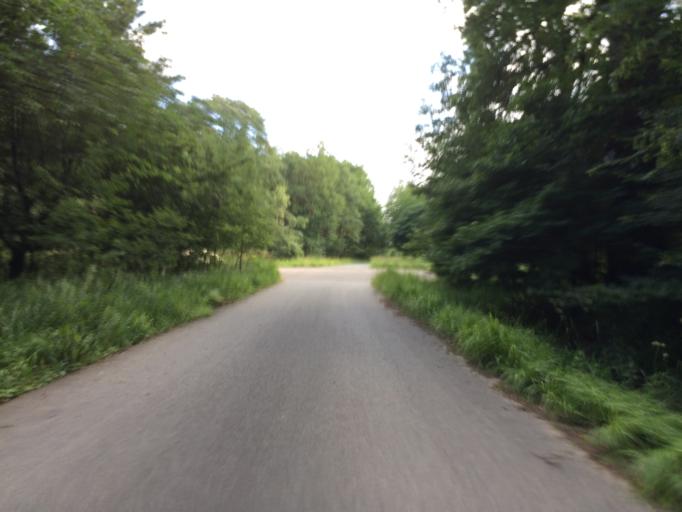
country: FR
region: Ile-de-France
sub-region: Departement de l'Essonne
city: Brunoy
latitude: 48.6676
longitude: 2.4855
